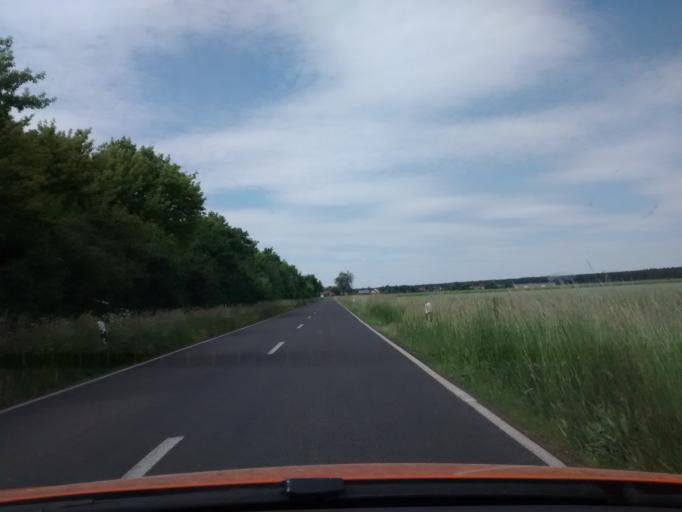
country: DE
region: Brandenburg
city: Ihlow
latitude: 51.9453
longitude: 13.3327
